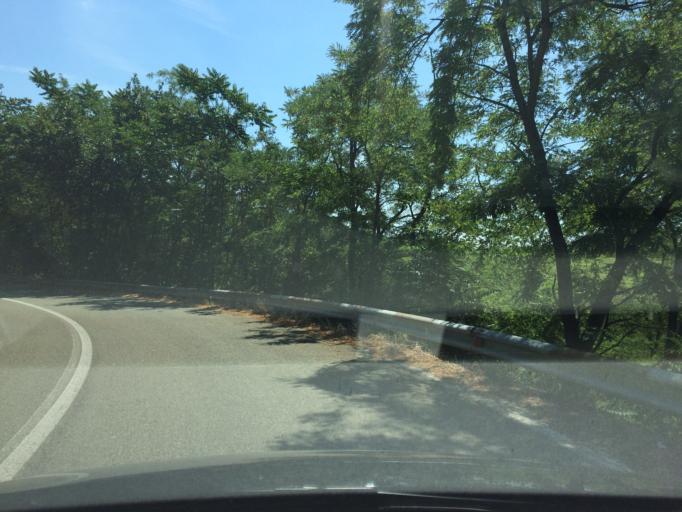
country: IT
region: Piedmont
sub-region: Provincia di Asti
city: Castel Rocchero
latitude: 44.7268
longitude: 8.4293
